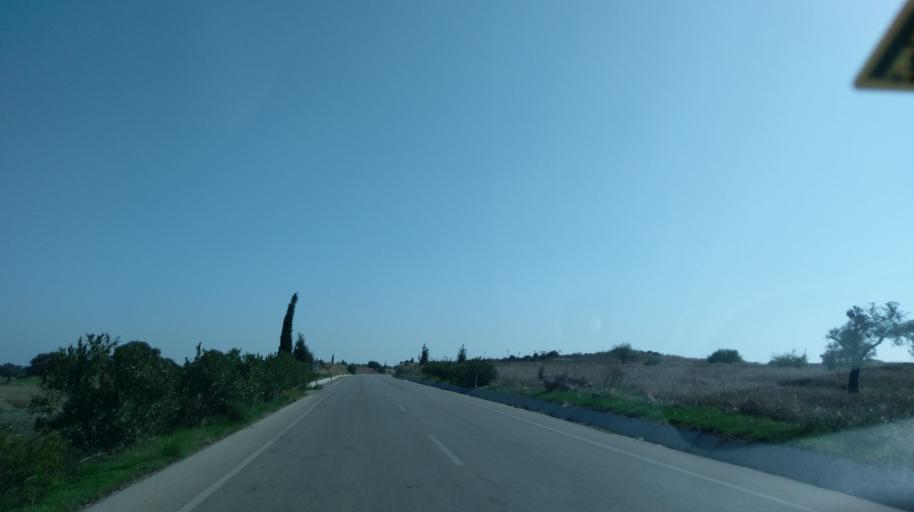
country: CY
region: Ammochostos
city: Leonarisso
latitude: 35.3929
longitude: 34.0069
